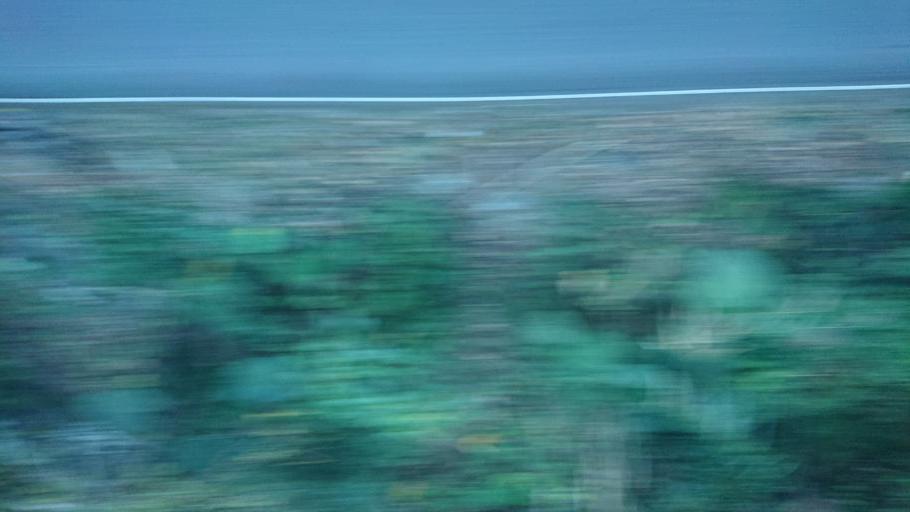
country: TW
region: Taiwan
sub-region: Chiayi
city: Jiayi Shi
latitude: 23.4654
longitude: 120.7184
